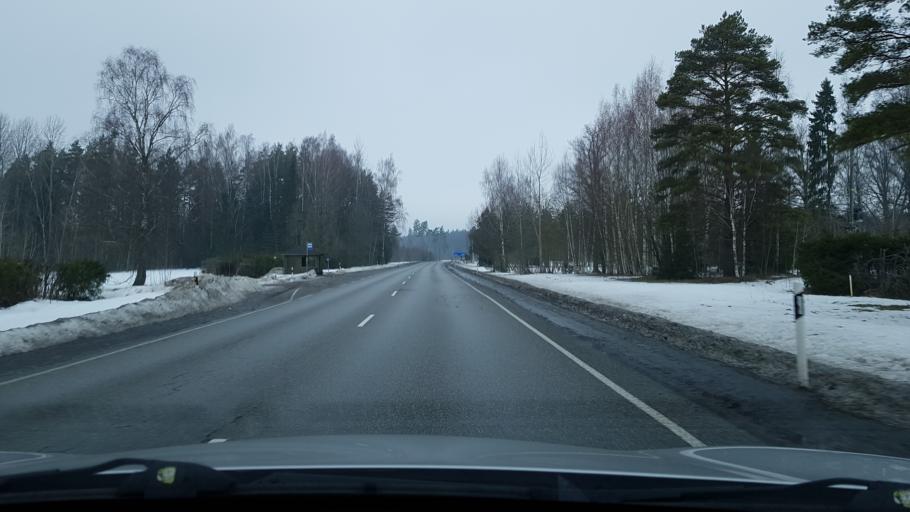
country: EE
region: Valgamaa
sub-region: Valga linn
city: Valga
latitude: 57.9489
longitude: 26.1678
